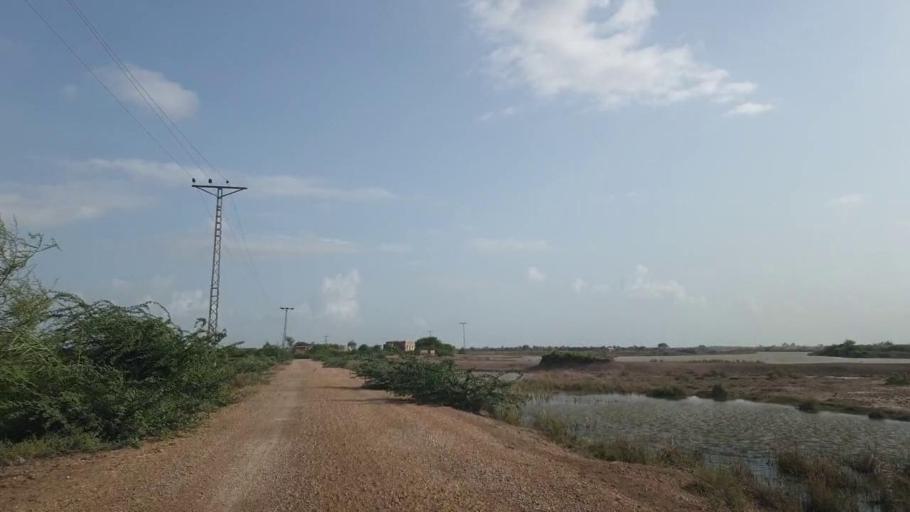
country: PK
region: Sindh
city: Kadhan
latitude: 24.6351
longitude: 69.0811
